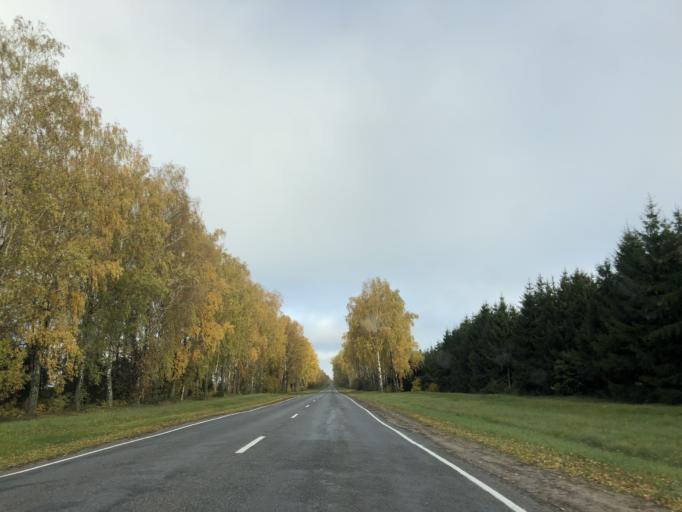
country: BY
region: Minsk
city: Uzda
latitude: 53.4771
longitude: 27.1884
